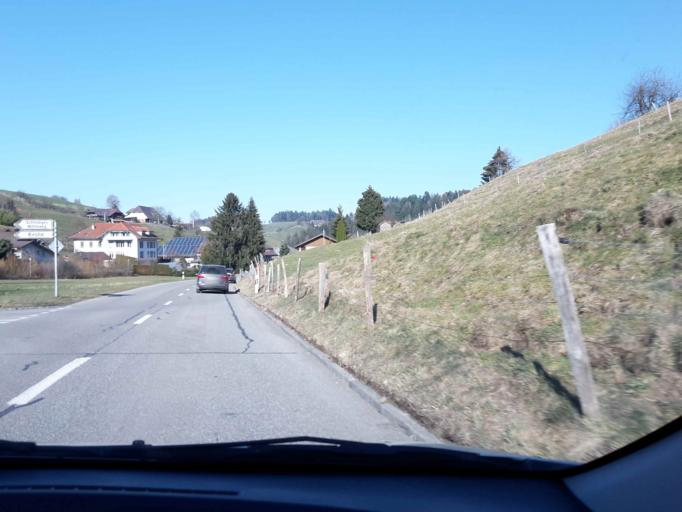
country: CH
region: Bern
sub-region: Emmental District
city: Durrenroth
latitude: 47.1114
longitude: 7.7773
